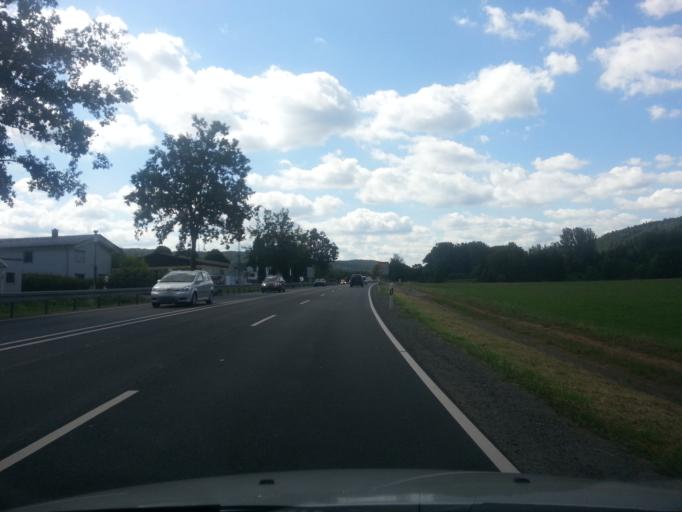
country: DE
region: Hesse
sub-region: Regierungsbezirk Darmstadt
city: Bad Konig
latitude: 49.7534
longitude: 9.0013
